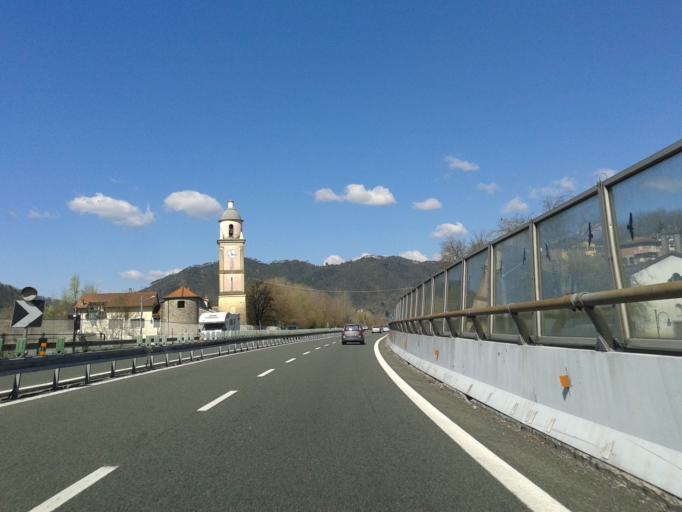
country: IT
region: Liguria
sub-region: Provincia di La Spezia
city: Beverino
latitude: 44.1987
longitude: 9.8114
